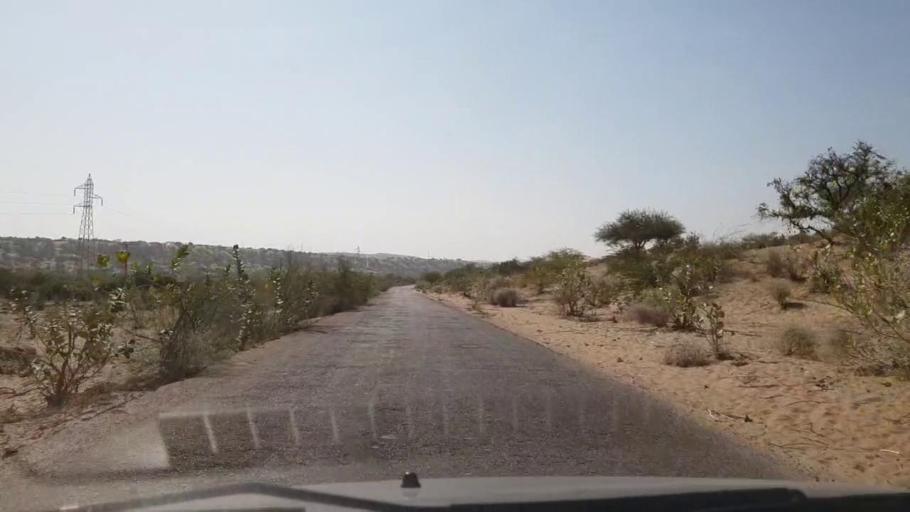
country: PK
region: Sindh
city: Diplo
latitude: 24.5403
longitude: 69.6445
